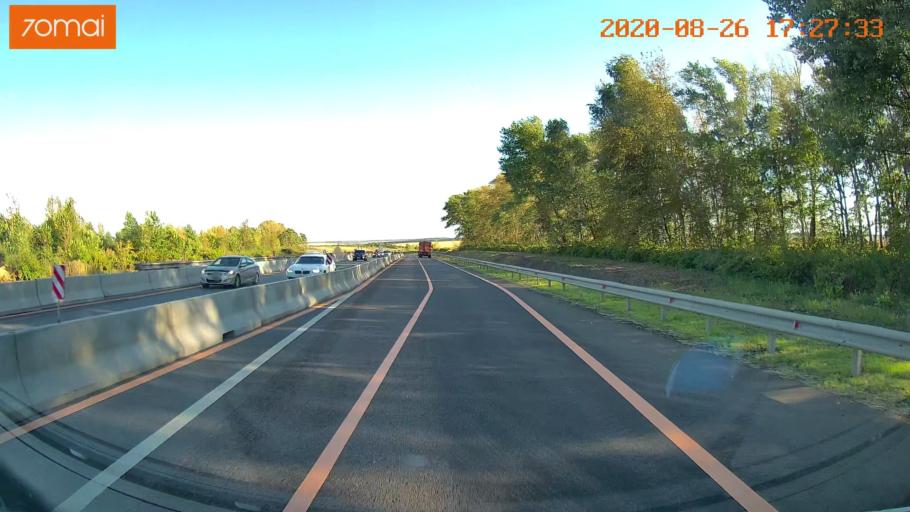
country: RU
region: Tula
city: Kazachka
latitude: 53.4717
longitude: 38.1252
